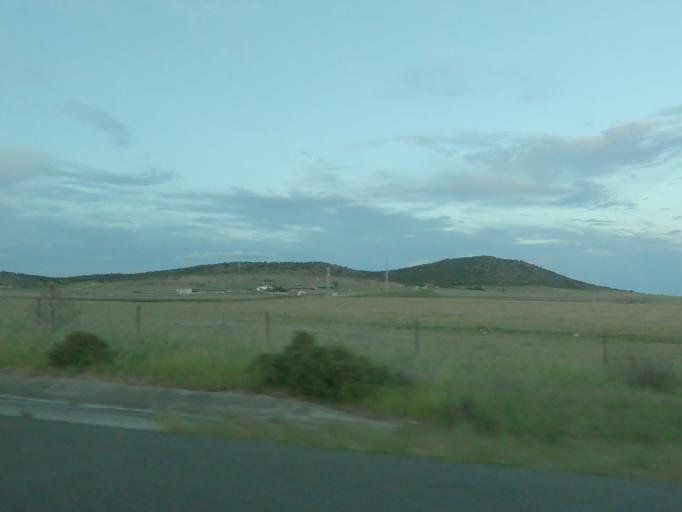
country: ES
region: Extremadura
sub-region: Provincia de Caceres
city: Caceres
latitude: 39.4131
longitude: -6.4020
